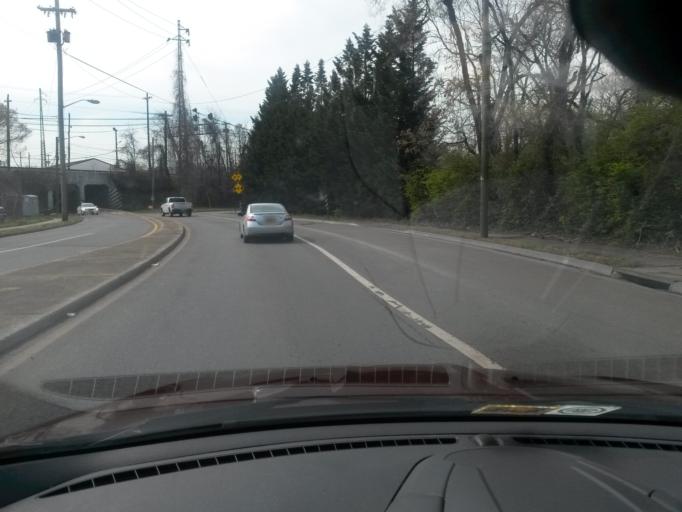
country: US
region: Virginia
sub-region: City of Roanoke
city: Roanoke
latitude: 37.2814
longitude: -79.9777
